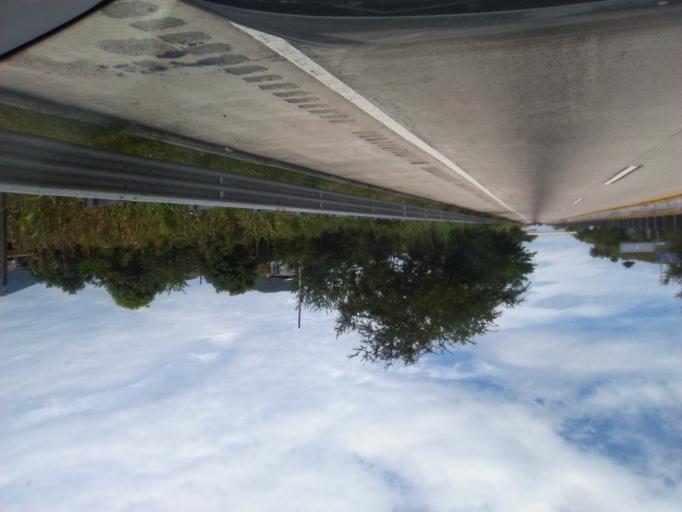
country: MX
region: Guerrero
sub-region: Chilpancingo de los Bravo
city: Julian Blanco (Dos Caminos)
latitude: 17.2227
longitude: -99.5283
